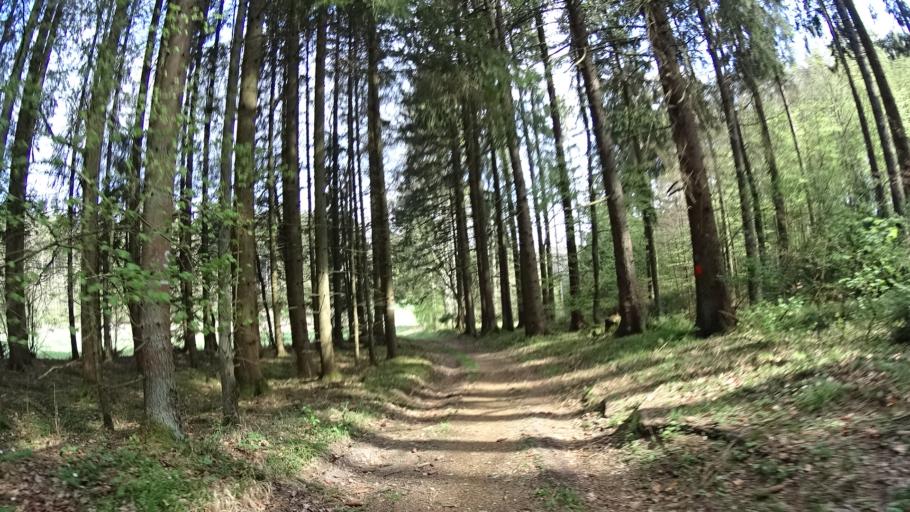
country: DE
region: Bavaria
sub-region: Upper Bavaria
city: Bohmfeld
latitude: 48.8587
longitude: 11.4034
